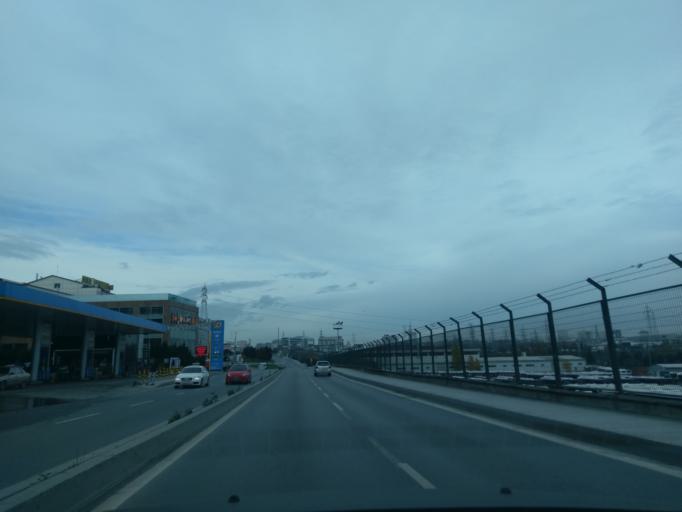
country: TR
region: Istanbul
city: Basaksehir
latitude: 41.0599
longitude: 28.7900
